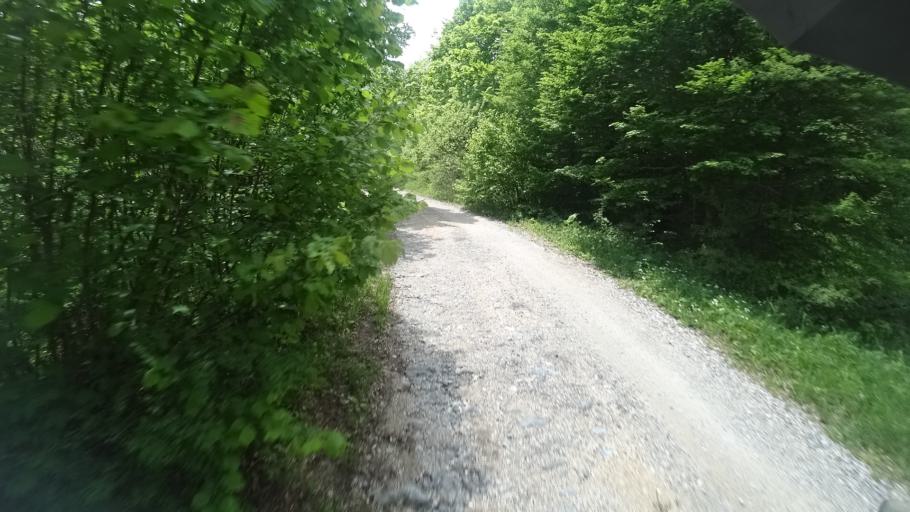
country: HR
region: Zadarska
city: Gracac
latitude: 44.4963
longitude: 15.8765
